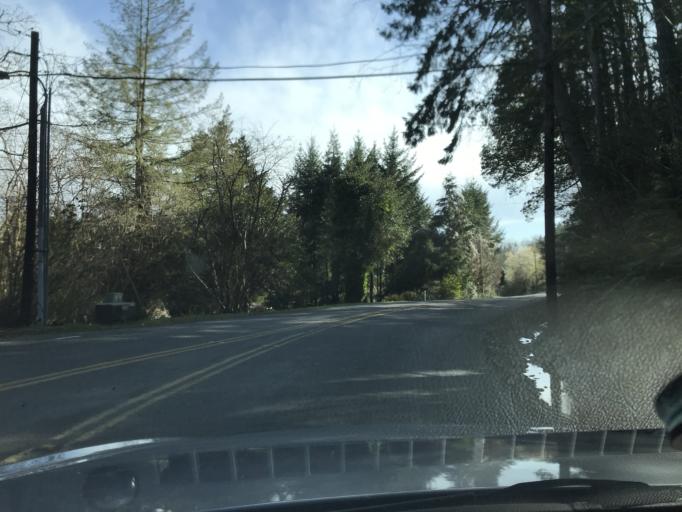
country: US
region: Washington
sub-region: Pierce County
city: Home
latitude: 47.2564
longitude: -122.7587
